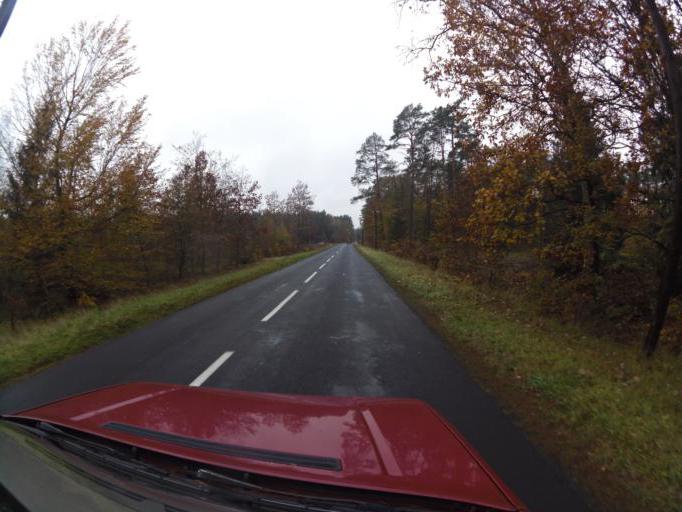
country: PL
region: West Pomeranian Voivodeship
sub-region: Powiat policki
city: Dobra
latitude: 53.5914
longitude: 14.3658
